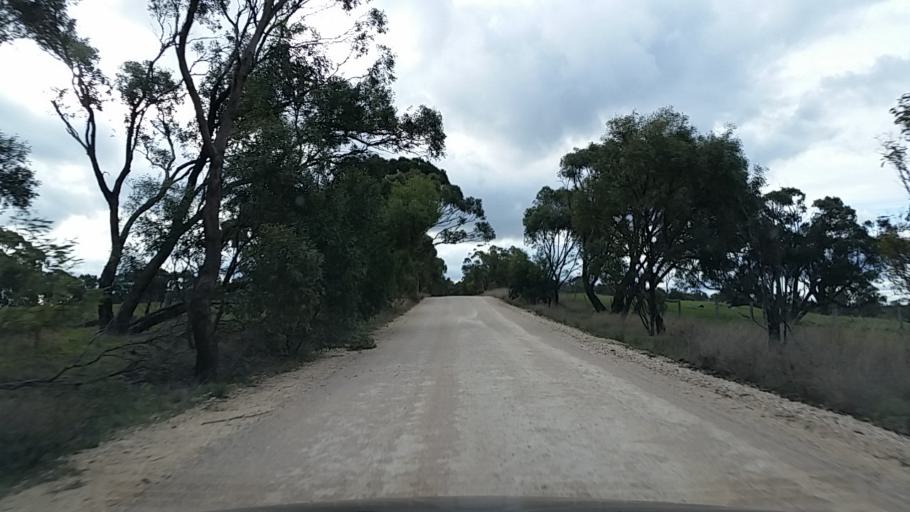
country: AU
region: South Australia
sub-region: Mount Barker
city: Callington
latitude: -35.0023
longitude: 139.0606
